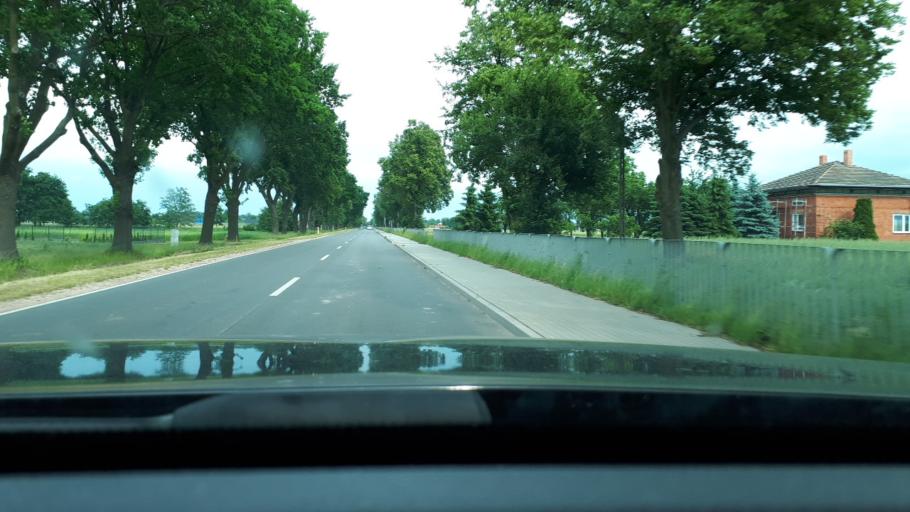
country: PL
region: Masovian Voivodeship
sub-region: Powiat warszawski zachodni
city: Kampinos
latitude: 52.2693
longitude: 20.4442
